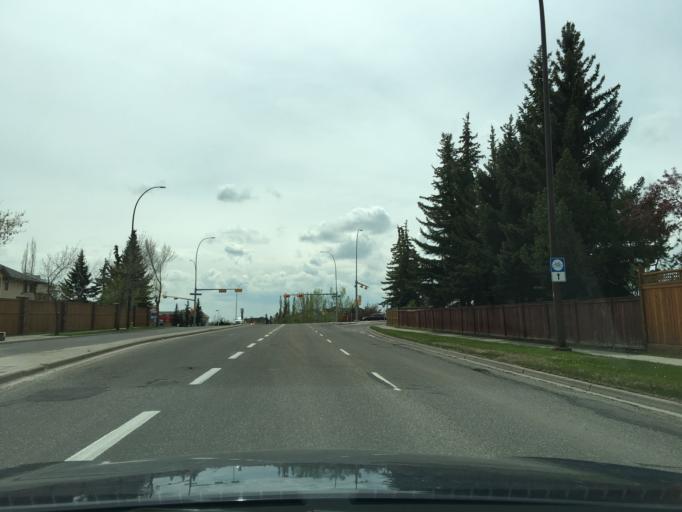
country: CA
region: Alberta
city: Calgary
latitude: 50.9404
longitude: -114.0856
